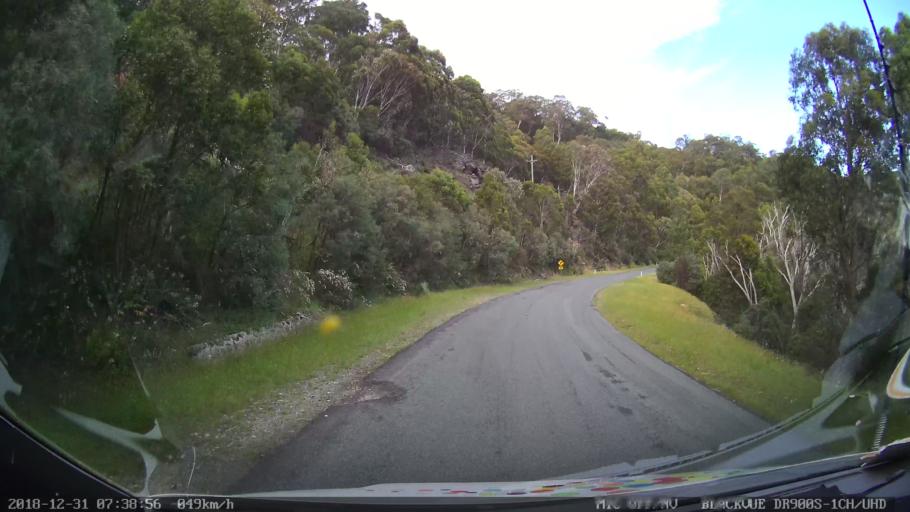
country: AU
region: New South Wales
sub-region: Snowy River
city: Jindabyne
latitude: -36.3498
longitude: 148.4251
